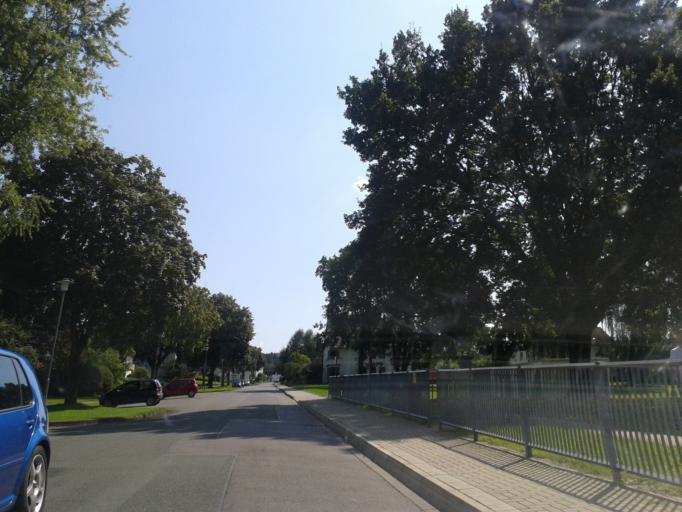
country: DE
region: North Rhine-Westphalia
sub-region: Regierungsbezirk Detmold
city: Schieder-Schwalenberg
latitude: 51.9169
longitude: 9.1547
